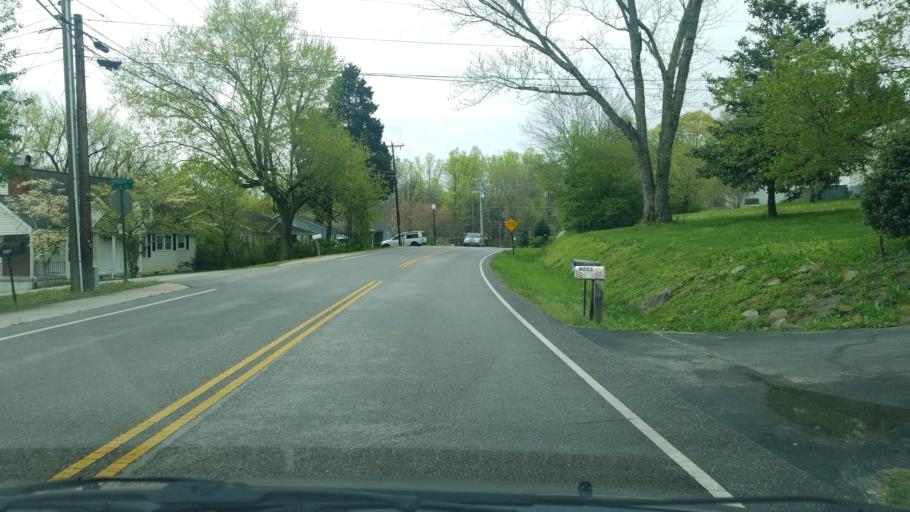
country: US
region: Tennessee
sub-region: Hamilton County
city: Collegedale
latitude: 35.0333
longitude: -85.0572
